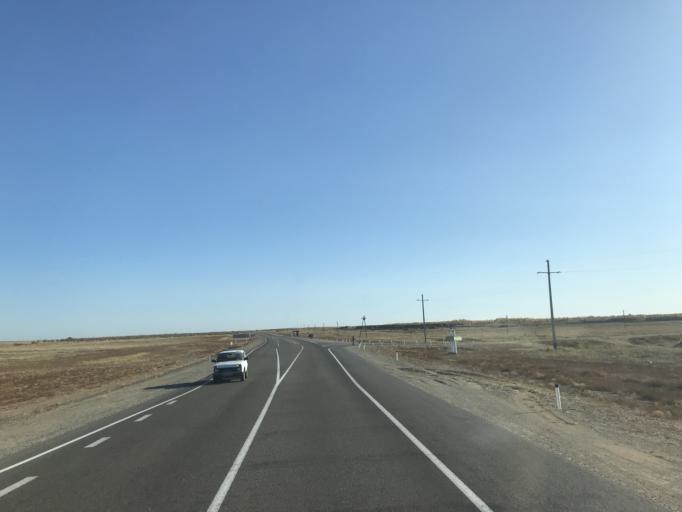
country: KZ
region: Pavlodar
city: Koktobe
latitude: 51.5400
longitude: 77.6456
